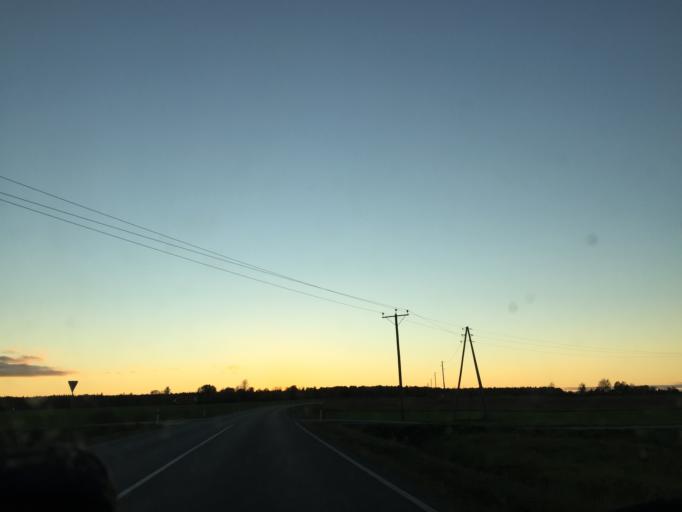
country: LV
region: Kandava
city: Kandava
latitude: 56.8963
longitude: 22.8721
